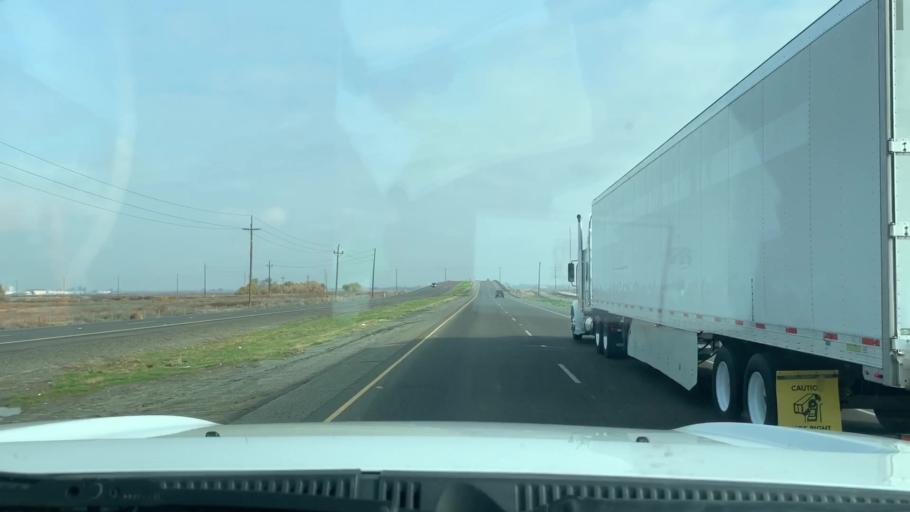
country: US
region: California
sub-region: Kings County
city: Lemoore Station
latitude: 36.2677
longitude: -119.8410
